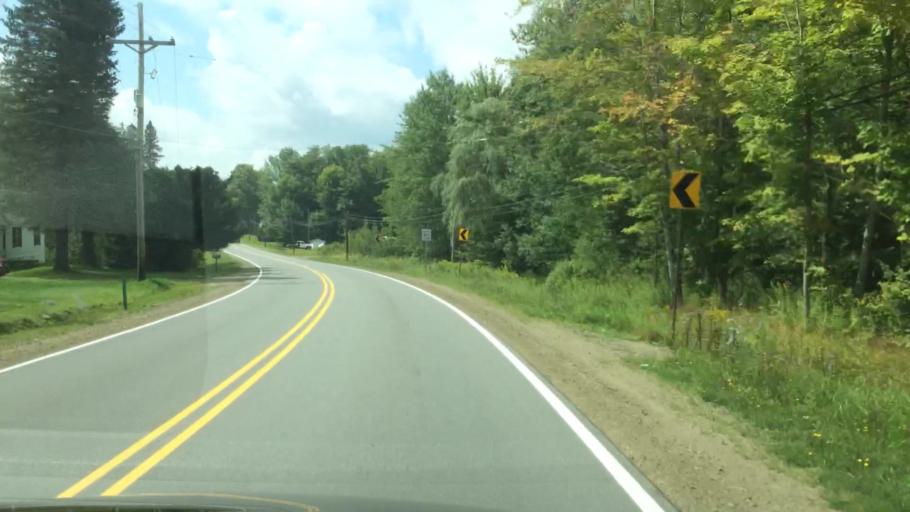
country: US
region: Pennsylvania
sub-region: McKean County
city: Bradford
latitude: 41.8724
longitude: -78.5884
